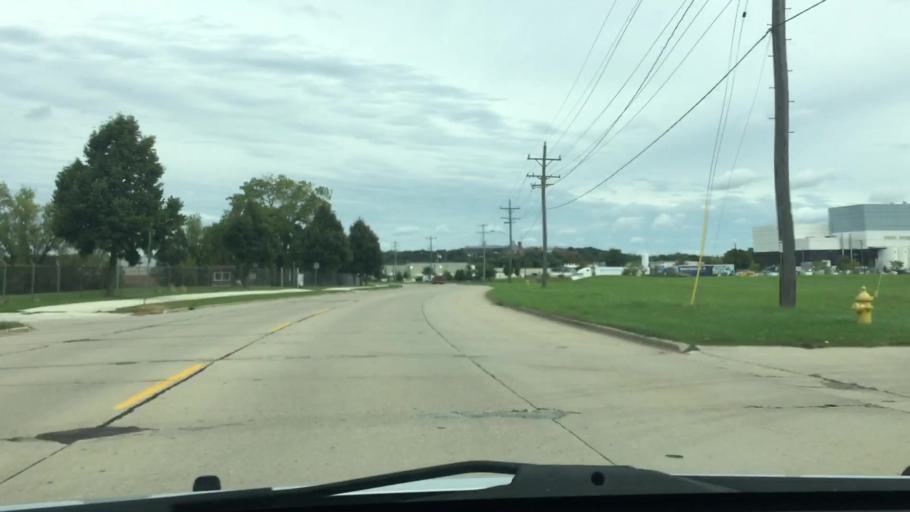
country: US
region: Wisconsin
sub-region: Waukesha County
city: Waukesha
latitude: 42.9943
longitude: -88.2497
